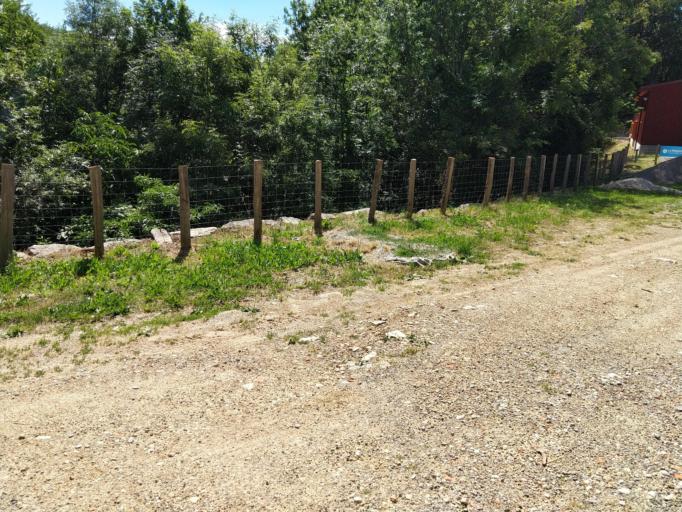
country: FR
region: Rhone-Alpes
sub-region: Departement de l'Ardeche
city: Saint-Priest
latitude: 44.7823
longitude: 4.4757
